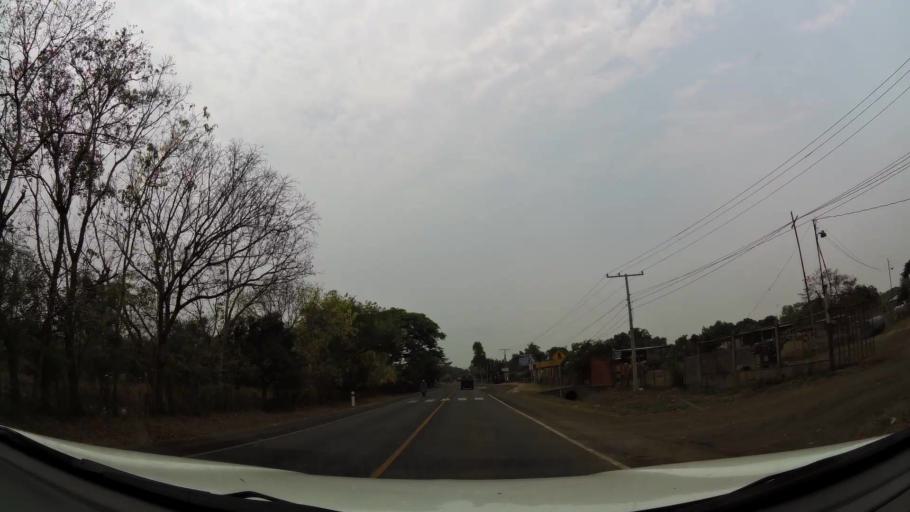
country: NI
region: Chinandega
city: Chinandega
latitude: 12.6144
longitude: -87.0944
